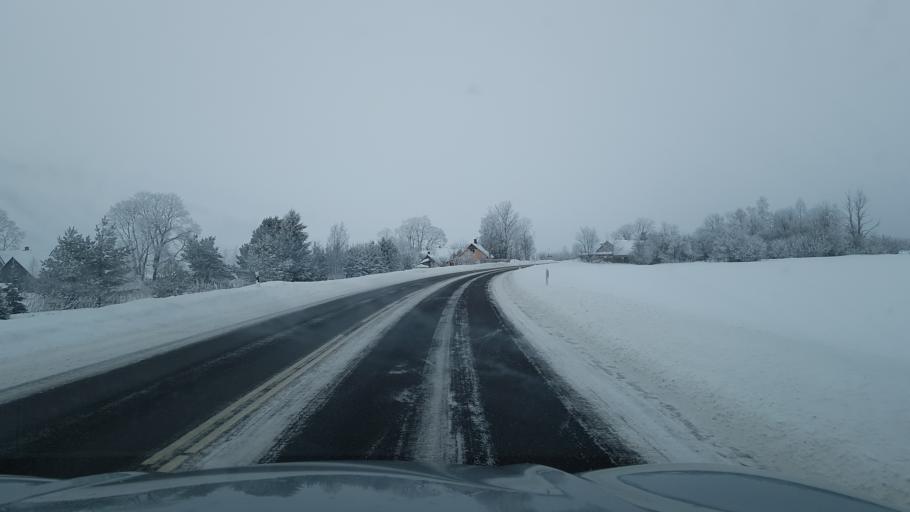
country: EE
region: Ida-Virumaa
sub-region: Johvi vald
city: Johvi
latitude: 59.3165
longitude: 27.3925
